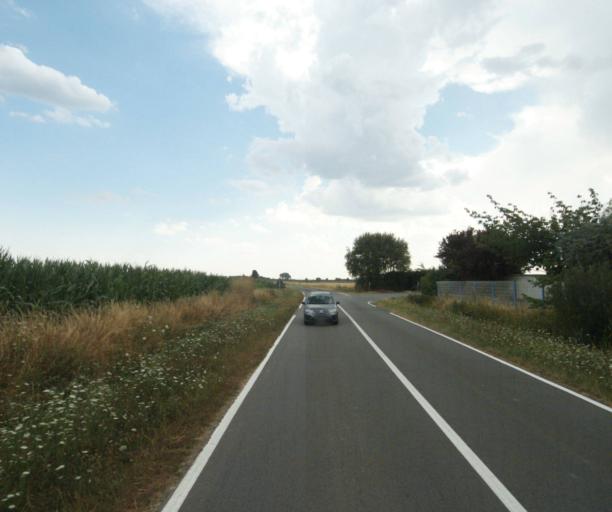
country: FR
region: Nord-Pas-de-Calais
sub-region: Departement du Nord
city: Deulemont
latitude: 50.7364
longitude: 2.9586
